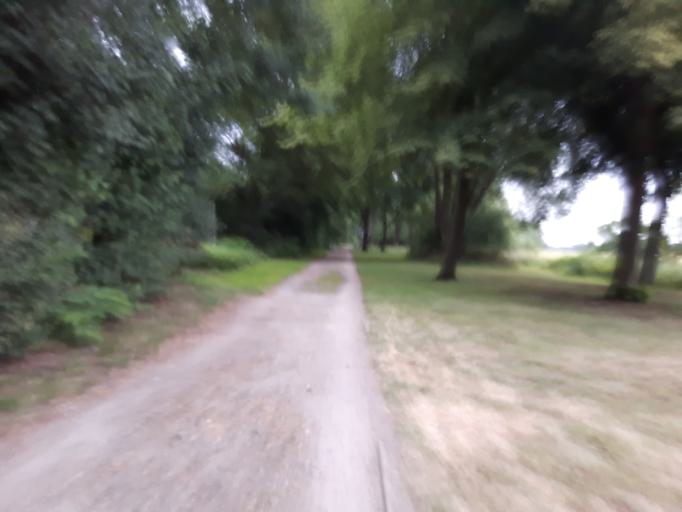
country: DE
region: Lower Saxony
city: Delmenhorst
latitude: 53.0178
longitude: 8.6628
